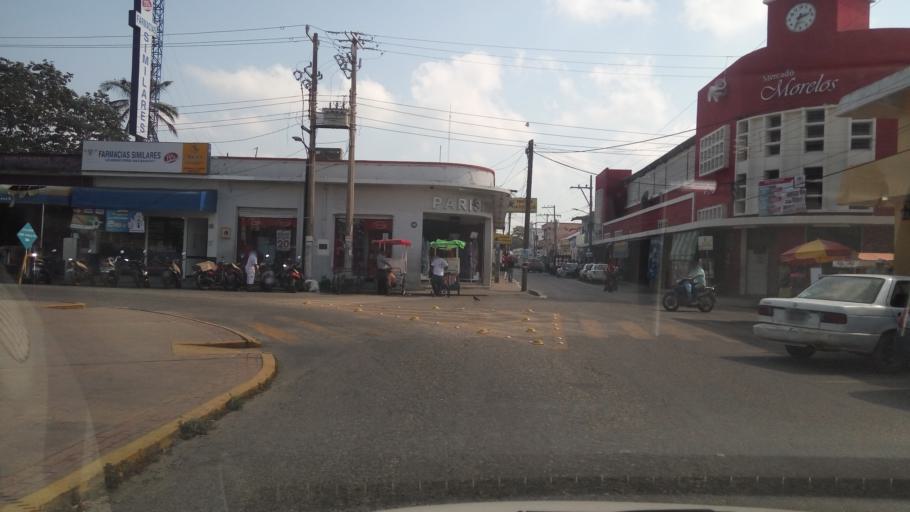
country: MX
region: Tabasco
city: Frontera
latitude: 18.5302
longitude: -92.6536
